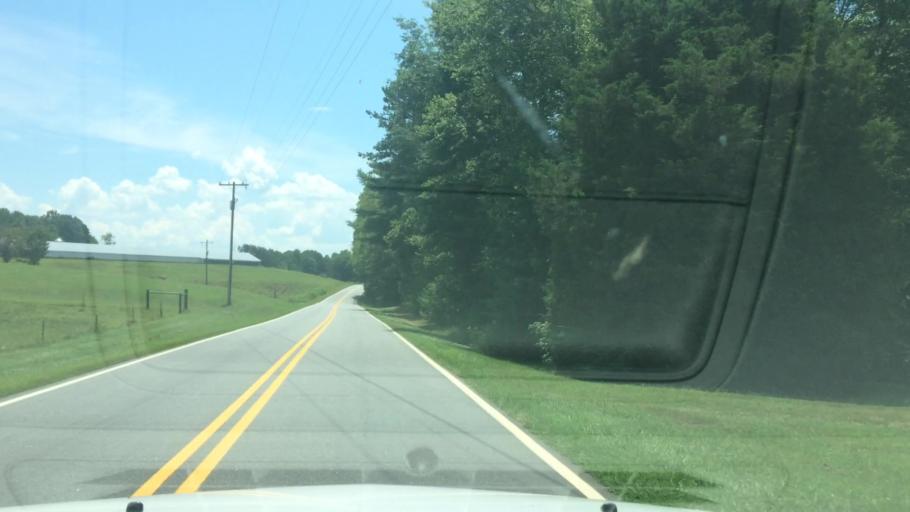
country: US
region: North Carolina
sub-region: Alexander County
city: Taylorsville
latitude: 35.9293
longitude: -81.2628
